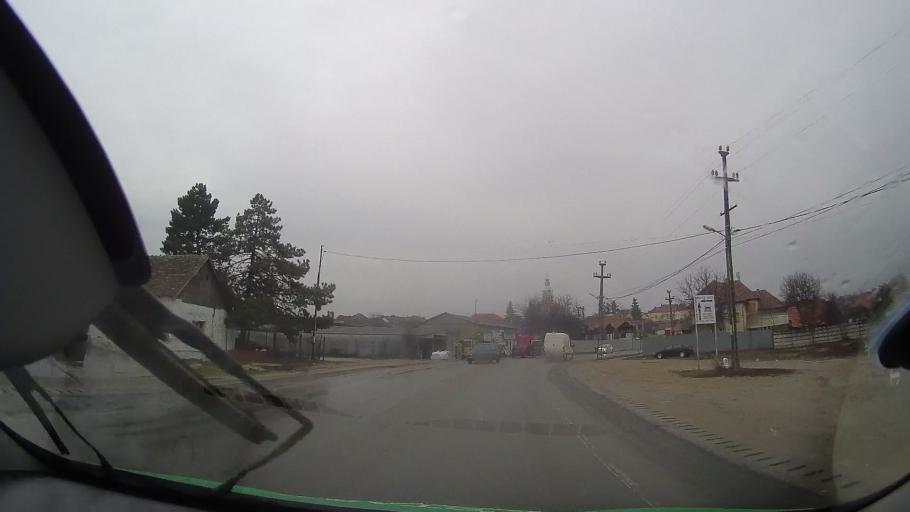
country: RO
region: Bihor
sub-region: Comuna Tinca
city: Tinca
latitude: 46.7711
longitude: 21.9307
